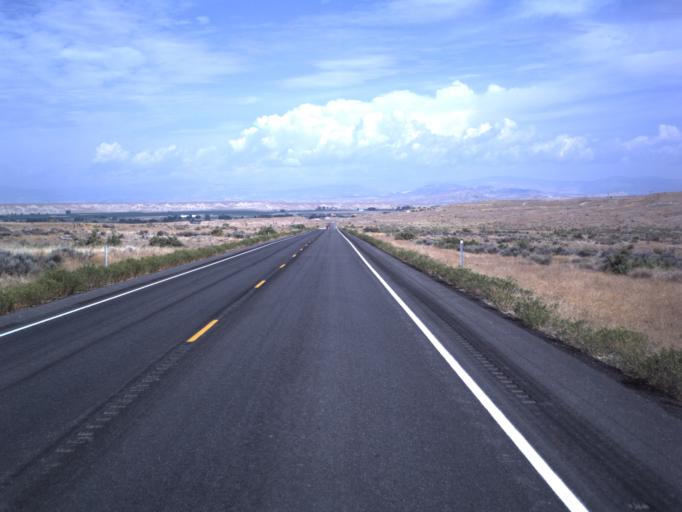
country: US
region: Utah
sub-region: Uintah County
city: Naples
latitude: 40.3569
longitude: -109.3137
